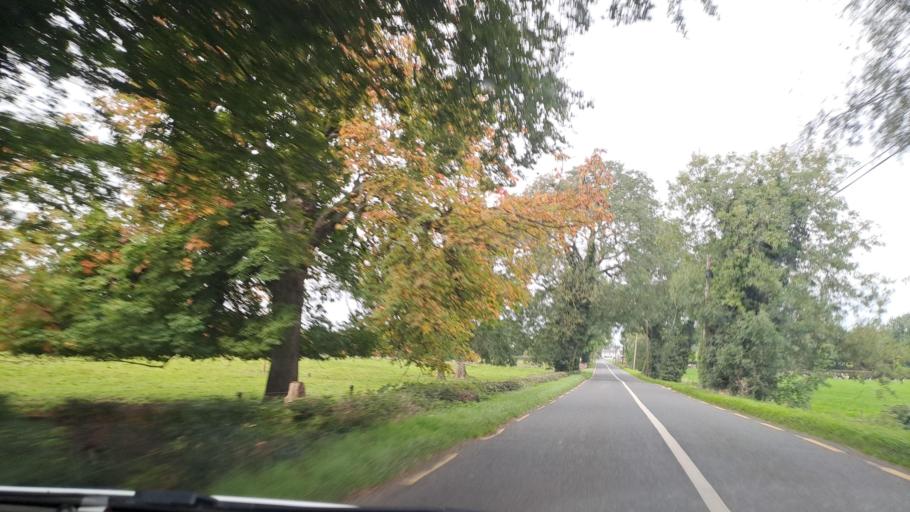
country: IE
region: Leinster
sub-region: Lu
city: Ardee
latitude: 53.8481
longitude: -6.6301
